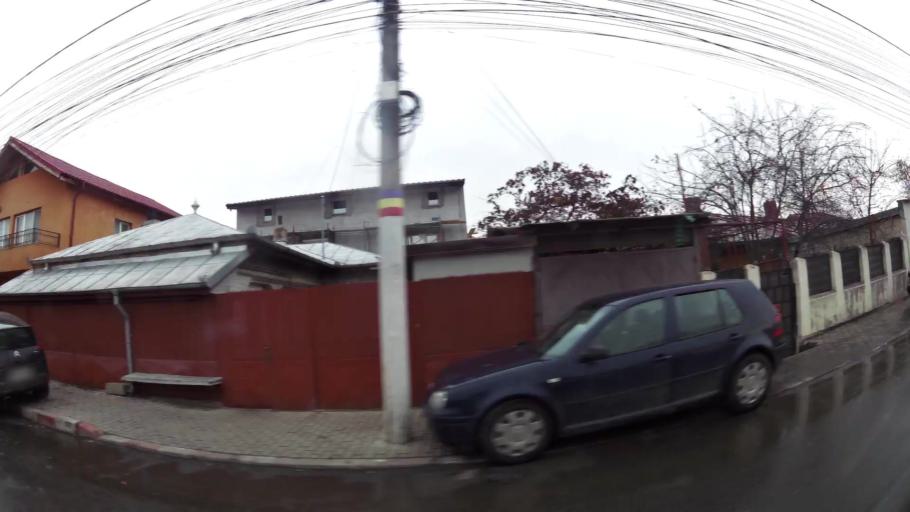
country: RO
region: Ilfov
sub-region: Voluntari City
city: Voluntari
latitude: 44.4834
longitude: 26.1701
